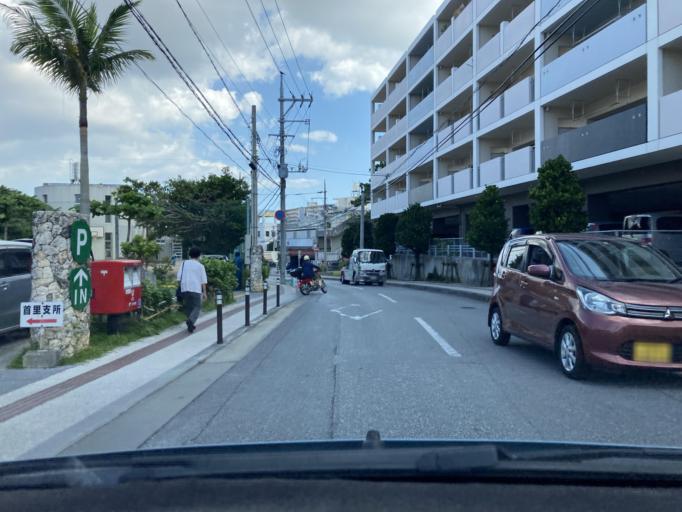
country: JP
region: Okinawa
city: Naha-shi
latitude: 26.2214
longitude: 127.7254
